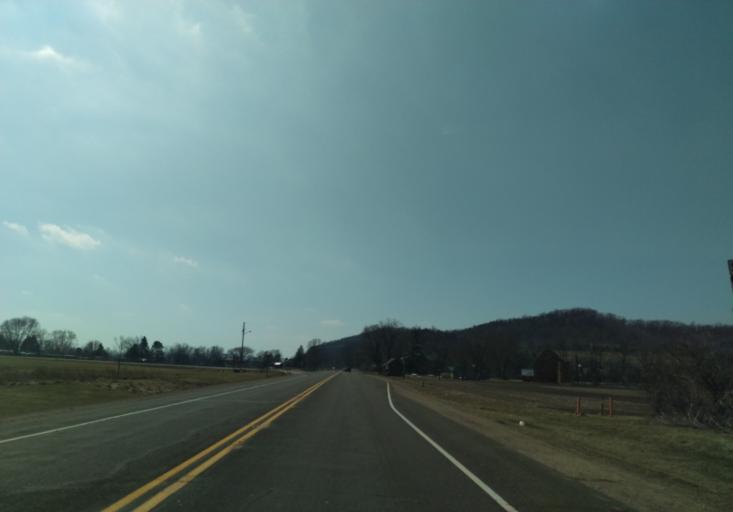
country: US
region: Wisconsin
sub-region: La Crosse County
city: La Crosse
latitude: 43.7612
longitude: -91.1837
